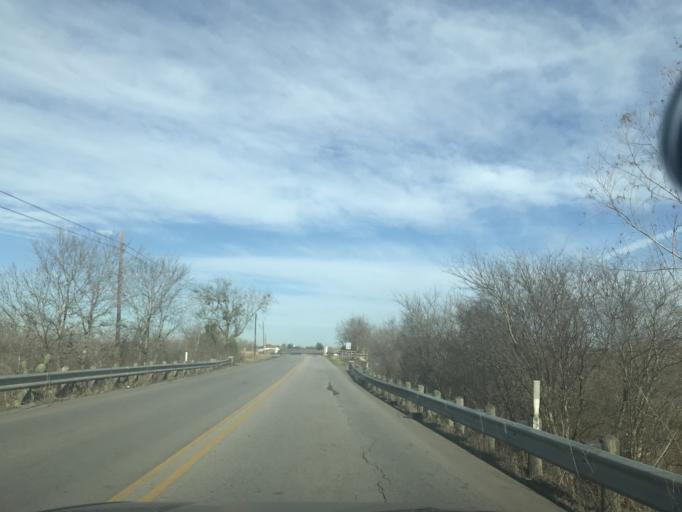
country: US
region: Texas
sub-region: Travis County
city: Manor
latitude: 30.3335
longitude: -97.5496
